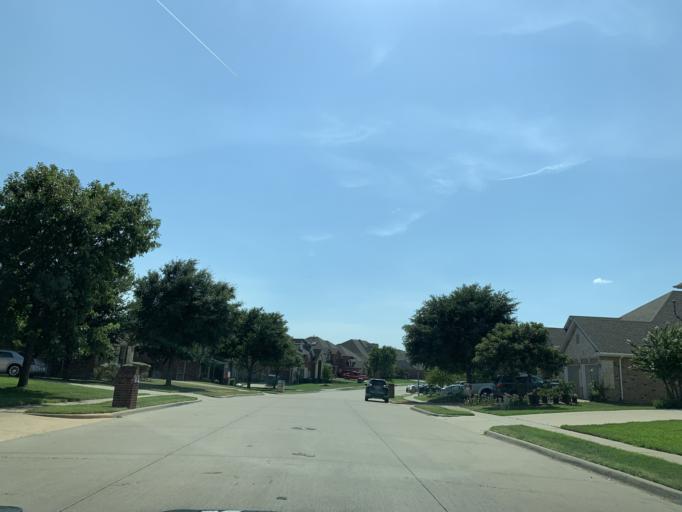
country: US
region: Texas
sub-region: Dallas County
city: Cedar Hill
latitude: 32.6507
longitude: -97.0011
